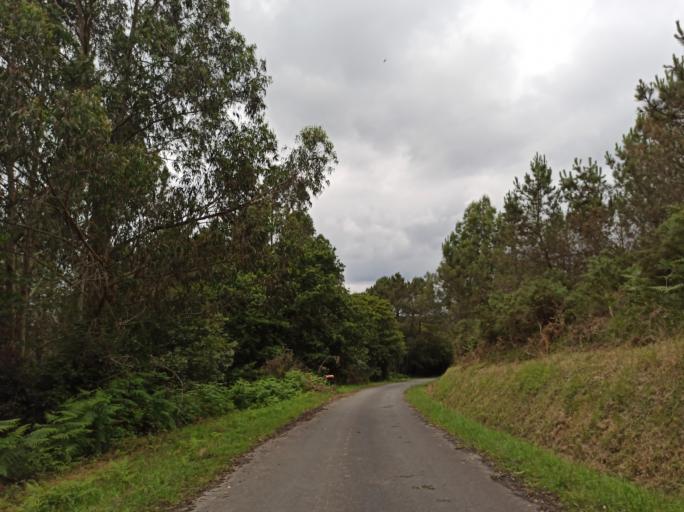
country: ES
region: Galicia
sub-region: Provincia de Pontevedra
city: Silleda
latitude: 42.7689
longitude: -8.1628
